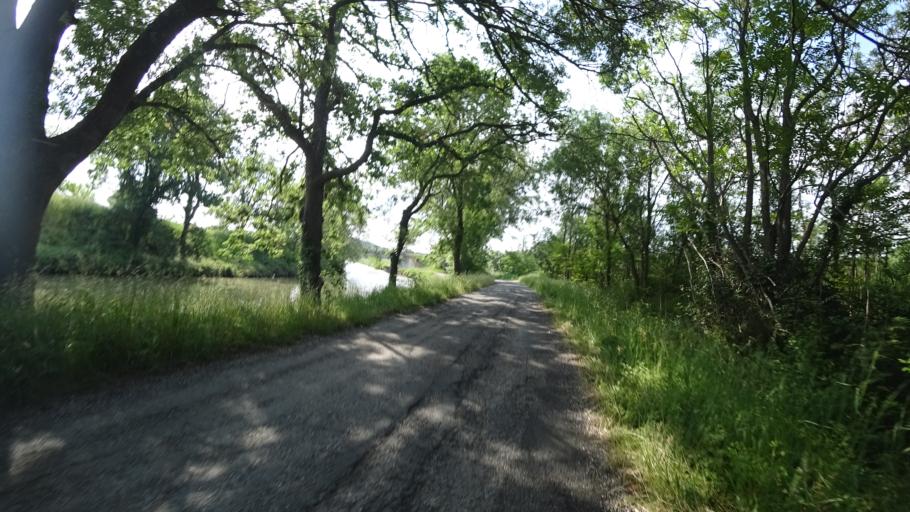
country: FR
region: Languedoc-Roussillon
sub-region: Departement de l'Herault
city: Olonzac
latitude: 43.2672
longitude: 2.7398
